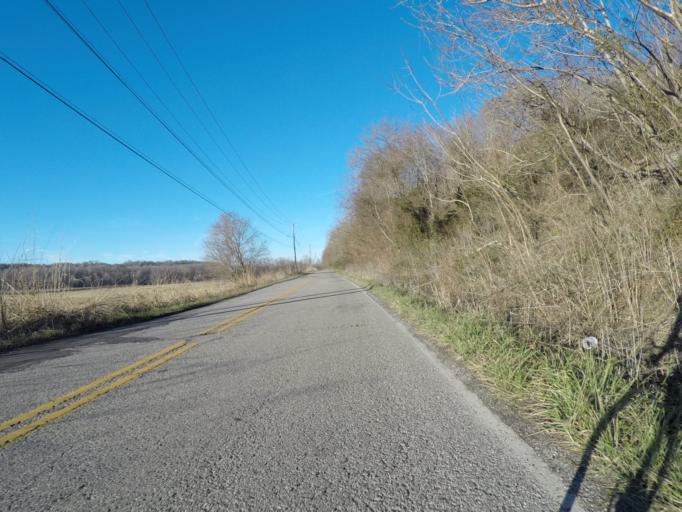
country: US
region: Kentucky
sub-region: Boyd County
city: Catlettsburg
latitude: 38.3903
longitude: -82.5932
